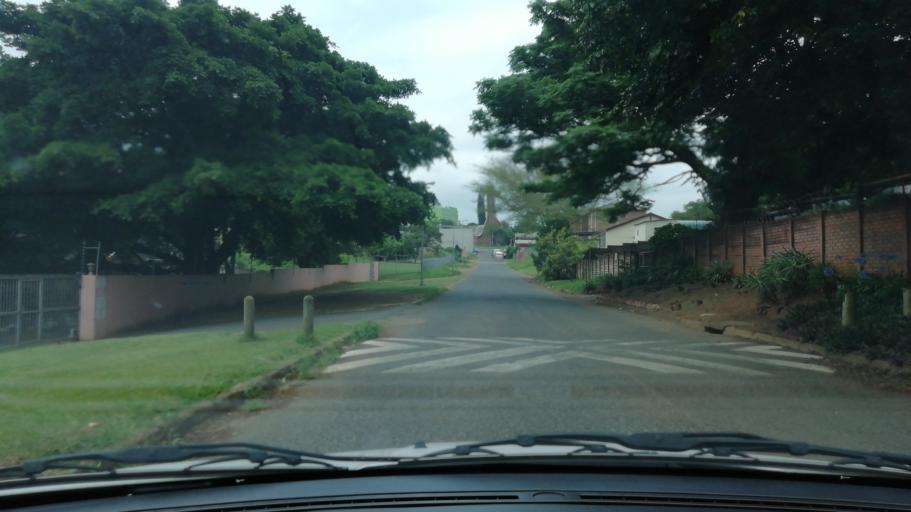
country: ZA
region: KwaZulu-Natal
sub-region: uThungulu District Municipality
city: Empangeni
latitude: -28.7489
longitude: 31.8907
